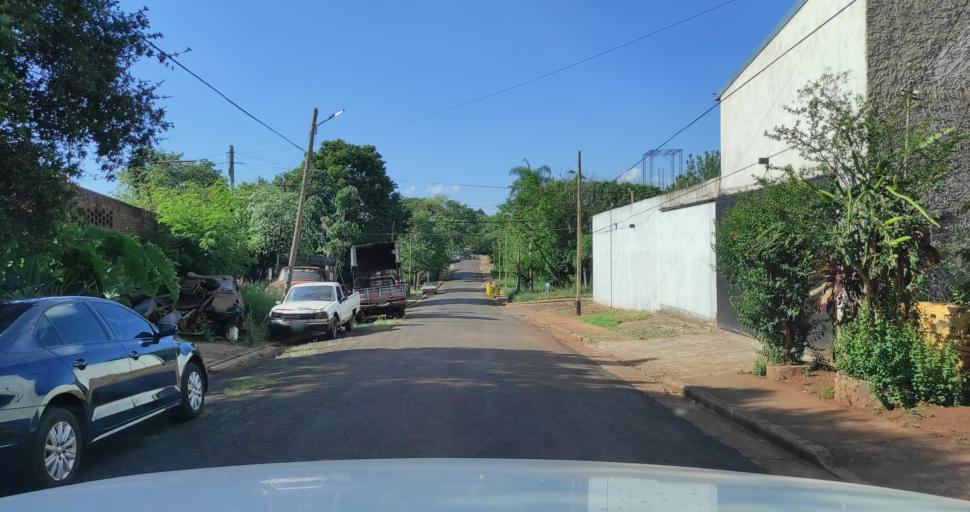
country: AR
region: Misiones
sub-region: Departamento de Capital
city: Posadas
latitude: -27.4151
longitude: -55.9259
